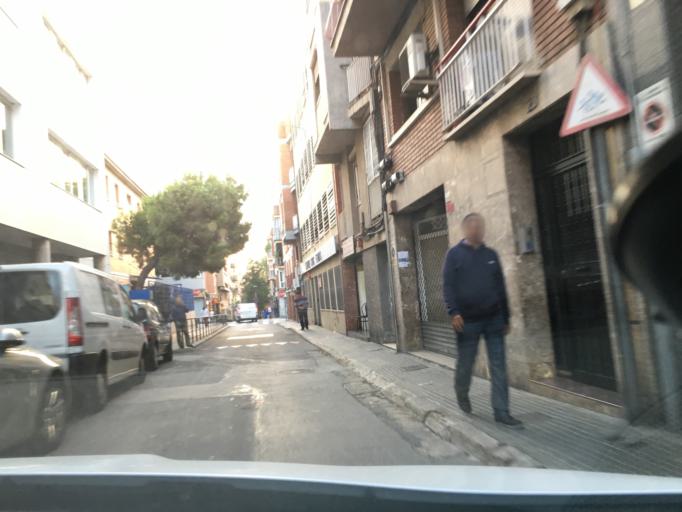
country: ES
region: Catalonia
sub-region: Provincia de Barcelona
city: Santa Coloma de Gramenet
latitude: 41.4508
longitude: 2.2204
